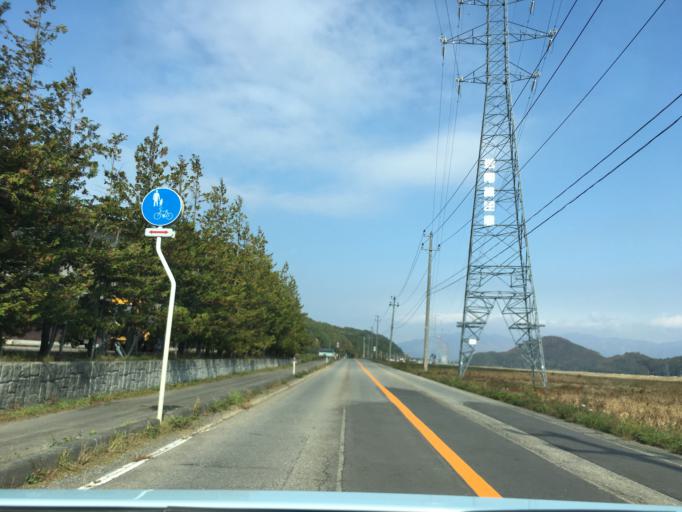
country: JP
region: Fukushima
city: Inawashiro
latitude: 37.4772
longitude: 140.0114
